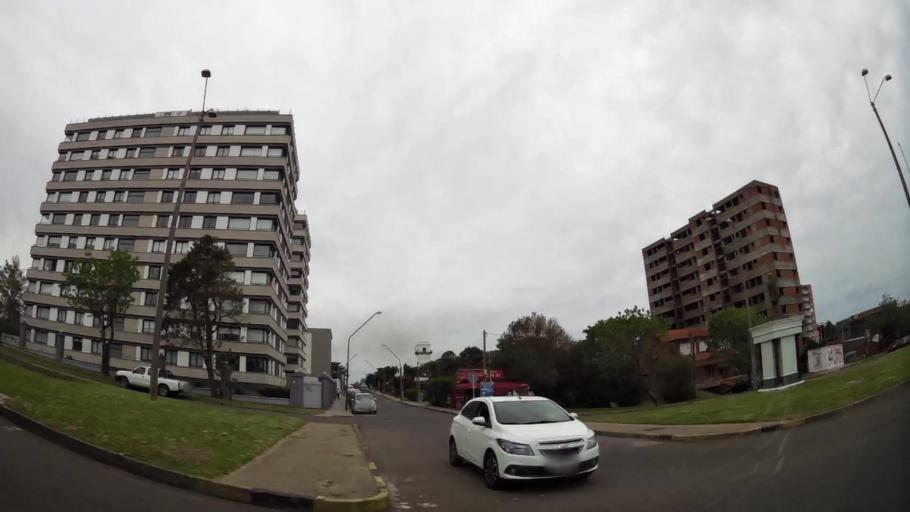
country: UY
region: Maldonado
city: Maldonado
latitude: -34.9103
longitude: -54.9634
